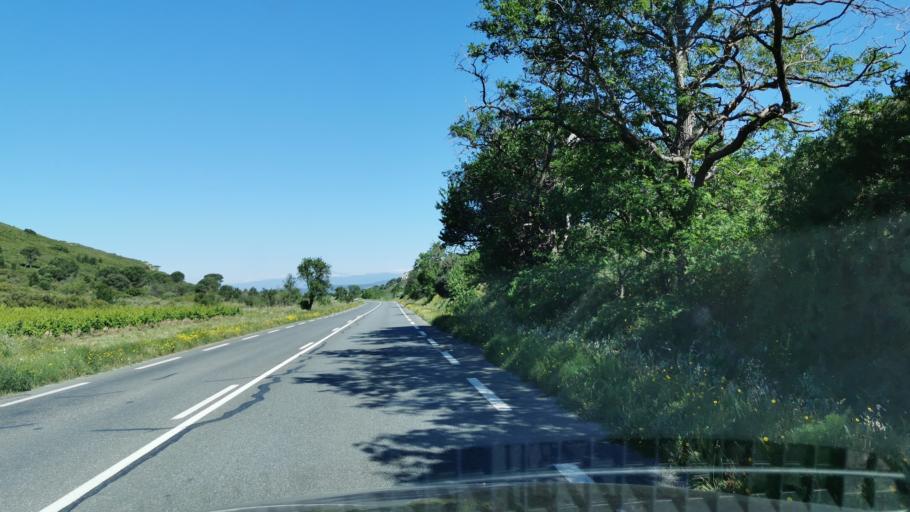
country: FR
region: Languedoc-Roussillon
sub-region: Departement de l'Aude
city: Nevian
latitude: 43.2036
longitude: 2.8896
